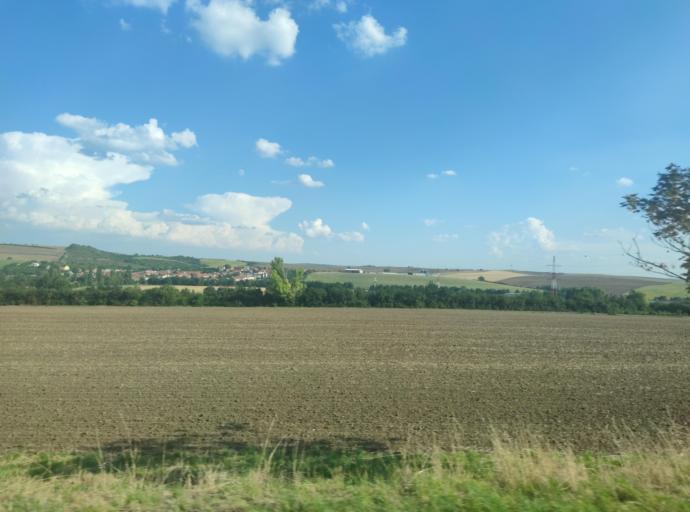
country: CZ
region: South Moravian
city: Vinicne Sumice
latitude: 49.1871
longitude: 16.8364
